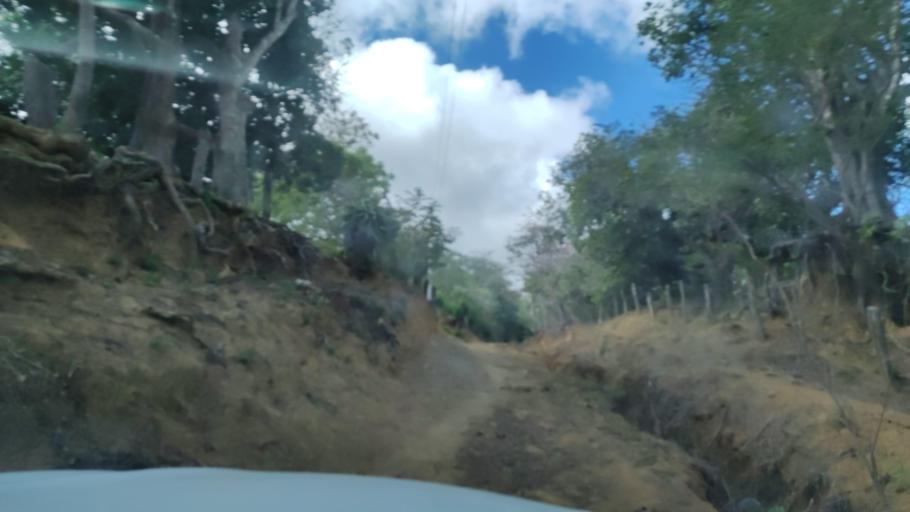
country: NI
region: Carazo
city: Santa Teresa
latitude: 11.6529
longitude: -86.1986
